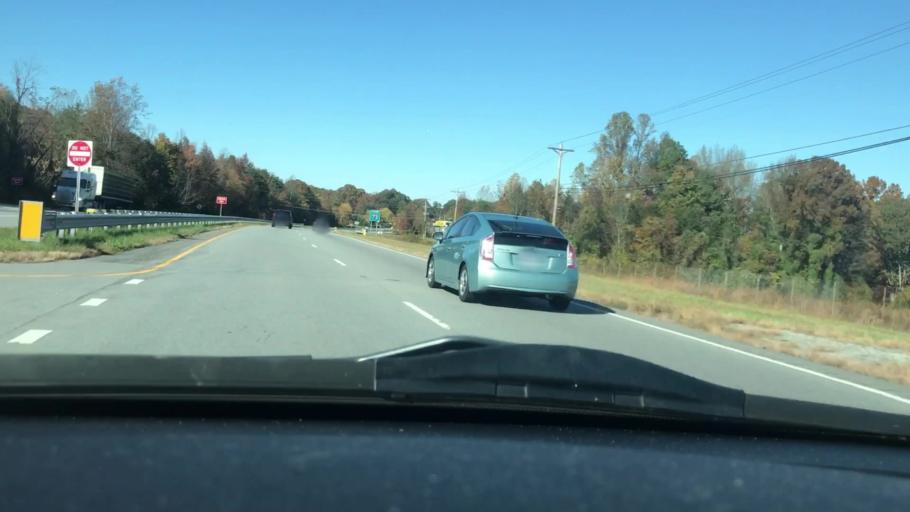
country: US
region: North Carolina
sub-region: Rockingham County
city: Madison
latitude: 36.3259
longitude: -79.9463
